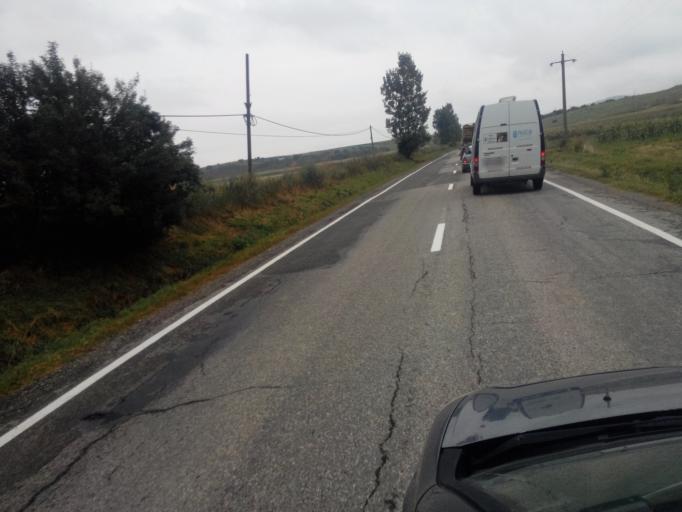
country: RO
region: Cluj
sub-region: Comuna Moldovenesti
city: Moldovenesti
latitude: 46.5106
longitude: 23.6651
